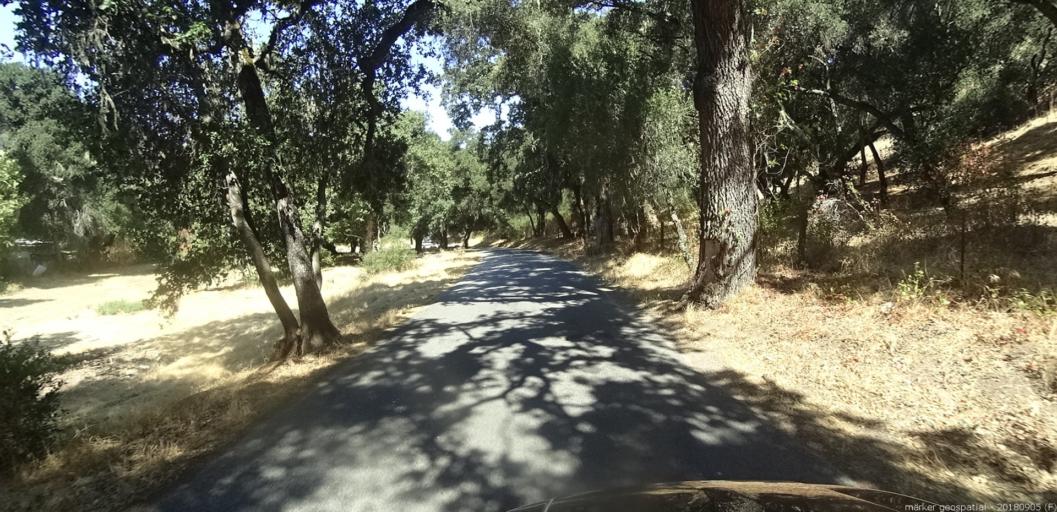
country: US
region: California
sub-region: Monterey County
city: Carmel Valley Village
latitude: 36.4009
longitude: -121.6567
